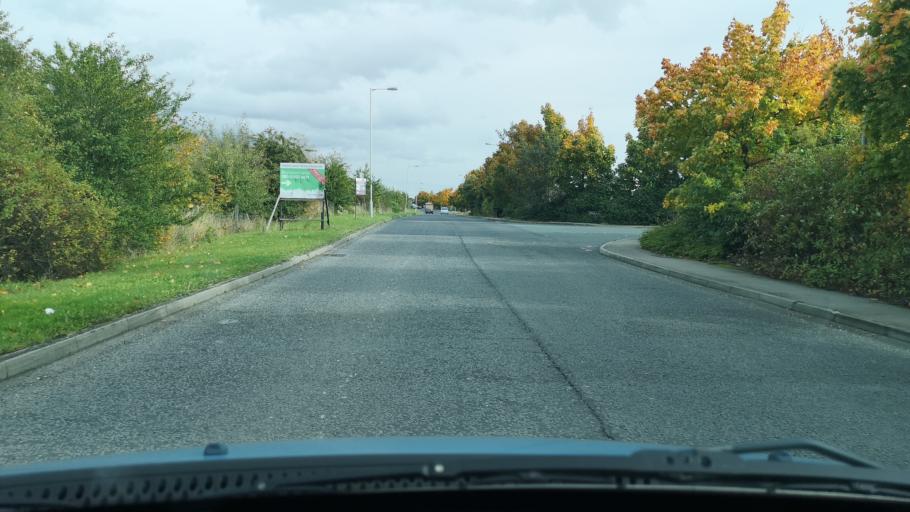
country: GB
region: England
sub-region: City and Borough of Wakefield
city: Featherstone
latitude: 53.6810
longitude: -1.3727
